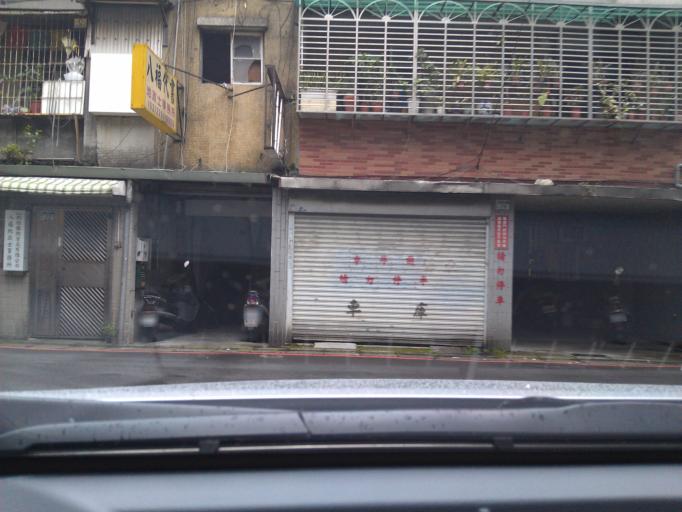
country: TW
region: Taipei
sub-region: Taipei
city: Banqiao
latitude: 25.0253
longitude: 121.4711
